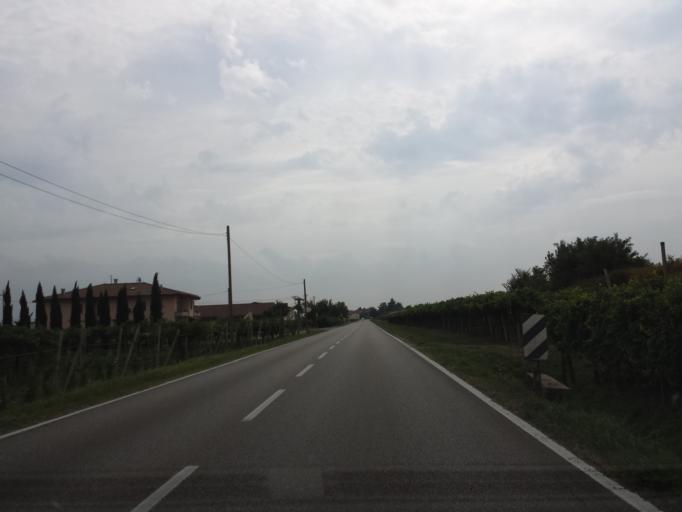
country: IT
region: Veneto
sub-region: Provincia di Verona
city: Brognoligo-Costalunga
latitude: 45.4593
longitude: 11.2977
